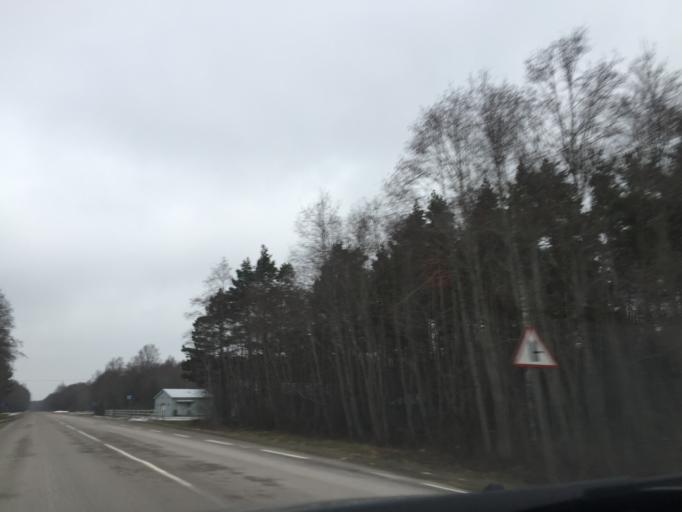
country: EE
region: Saare
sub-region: Kuressaare linn
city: Kuressaare
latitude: 58.2911
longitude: 22.3831
